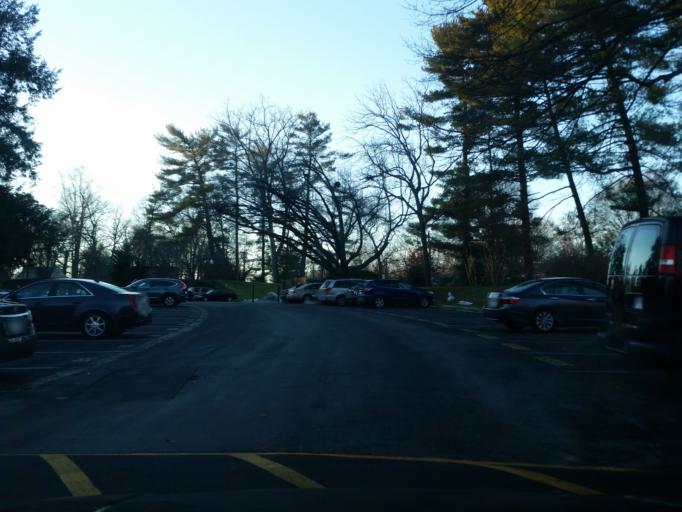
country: US
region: Maryland
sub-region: Montgomery County
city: Chevy Chase
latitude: 38.9724
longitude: -77.0547
